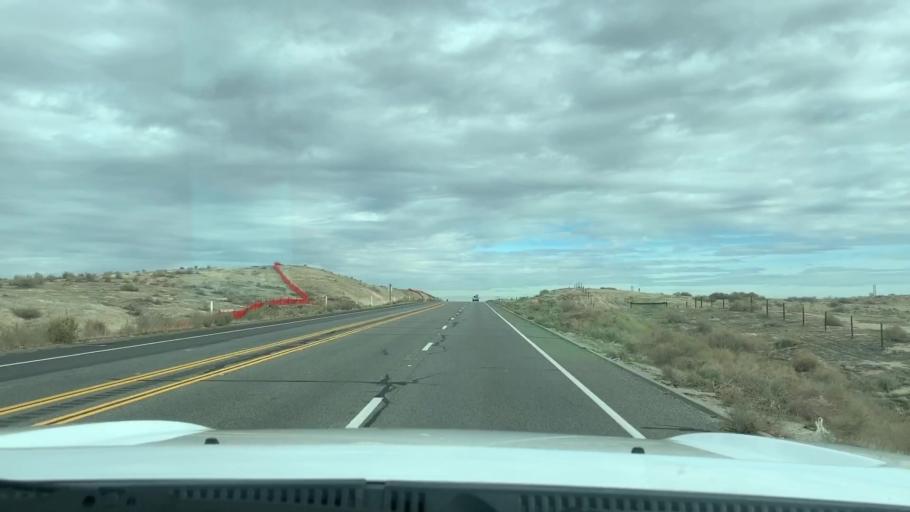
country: US
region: California
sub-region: Kern County
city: Ford City
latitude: 35.2537
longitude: -119.3334
